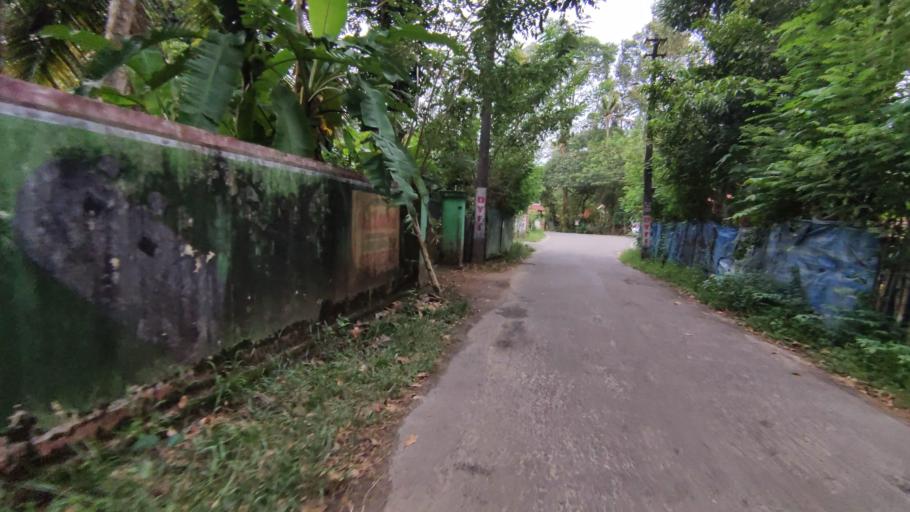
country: IN
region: Kerala
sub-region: Alappuzha
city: Shertallai
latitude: 9.6546
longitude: 76.3691
